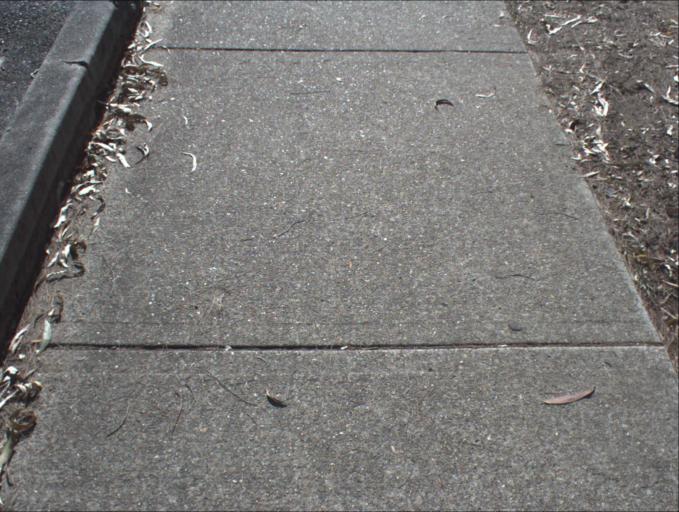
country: AU
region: Queensland
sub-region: Logan
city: Beenleigh
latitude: -27.6948
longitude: 153.2126
